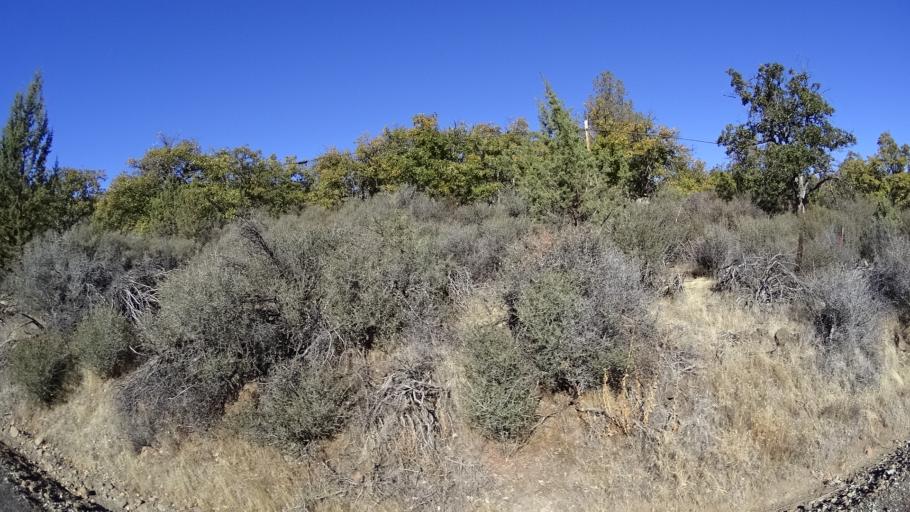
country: US
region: California
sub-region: Siskiyou County
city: Montague
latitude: 41.9594
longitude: -122.3198
